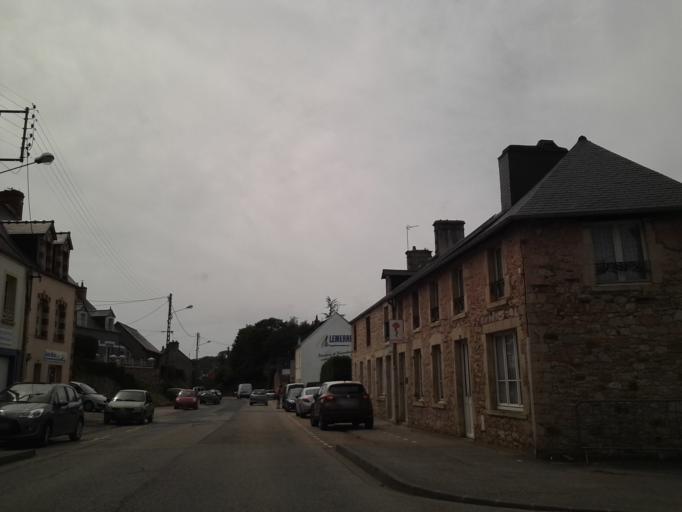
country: FR
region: Lower Normandy
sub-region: Departement de la Manche
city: Bricquebec
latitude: 49.4694
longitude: -1.6331
